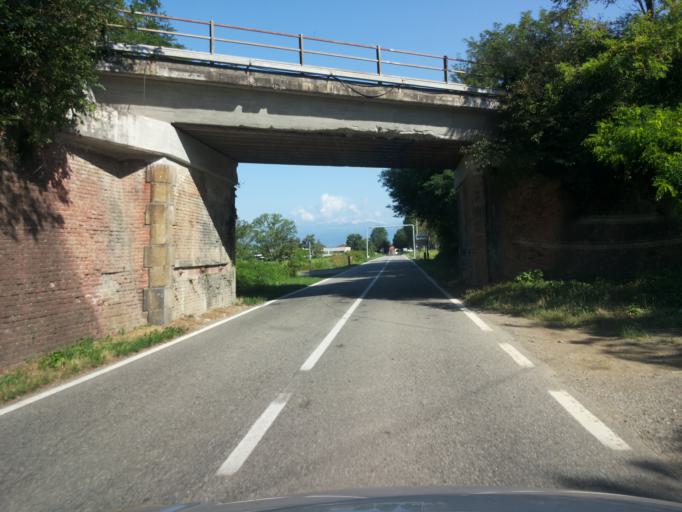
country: IT
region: Piedmont
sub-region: Provincia di Vercelli
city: Buronzo
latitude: 45.4735
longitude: 8.2681
